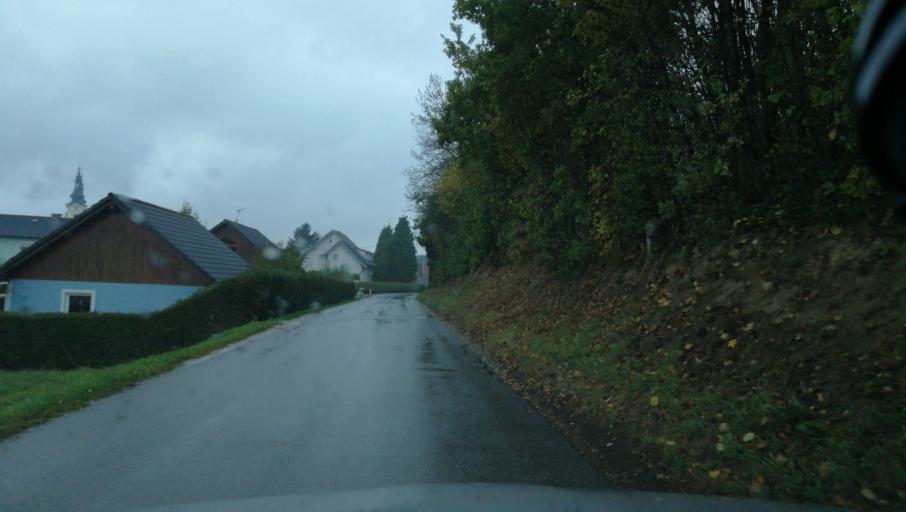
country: AT
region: Styria
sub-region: Politischer Bezirk Leibnitz
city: Sankt Veit am Vogau
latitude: 46.7463
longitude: 15.6307
